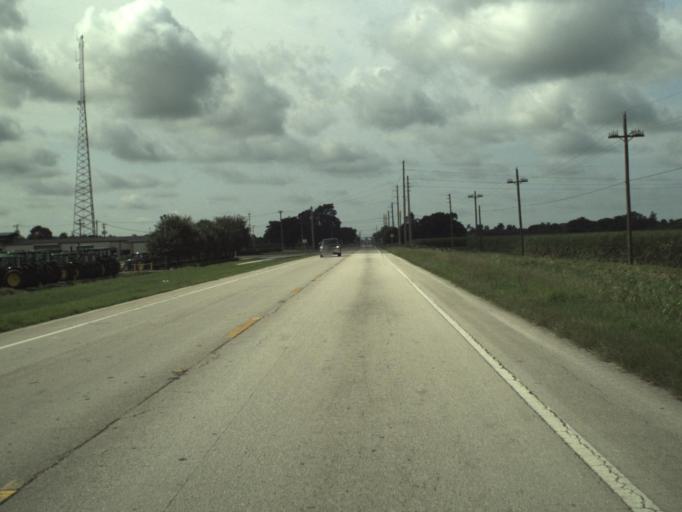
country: US
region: Florida
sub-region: Palm Beach County
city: Belle Glade
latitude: 26.7064
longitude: -80.6841
